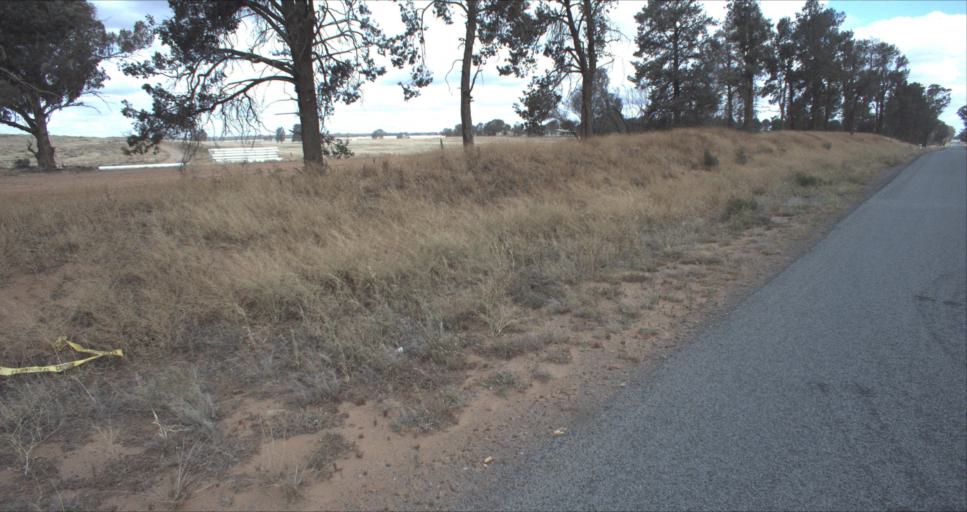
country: AU
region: New South Wales
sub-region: Leeton
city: Leeton
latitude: -34.6583
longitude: 146.3498
